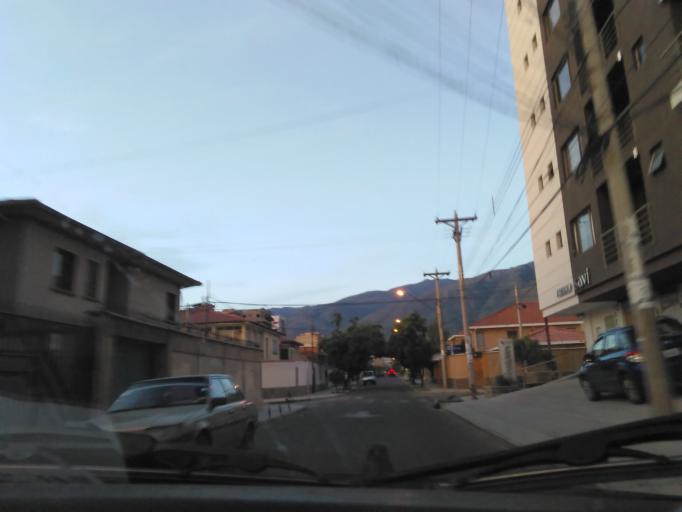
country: BO
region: Cochabamba
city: Cochabamba
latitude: -17.3776
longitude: -66.1654
